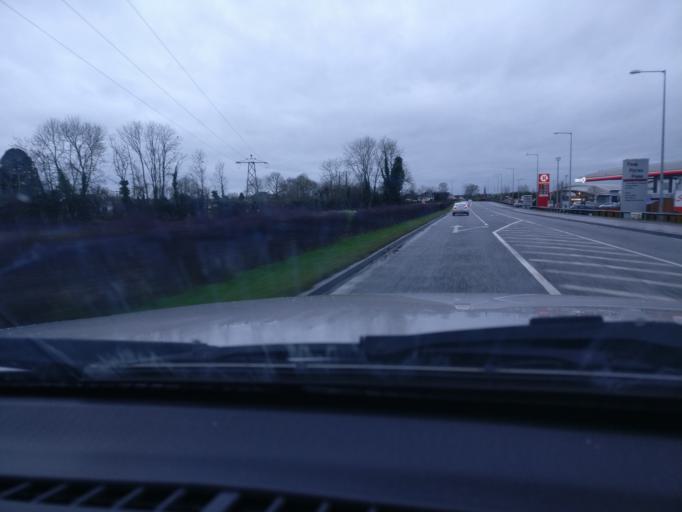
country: IE
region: Leinster
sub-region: An Mhi
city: Newtown Trim
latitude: 53.5627
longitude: -6.7653
